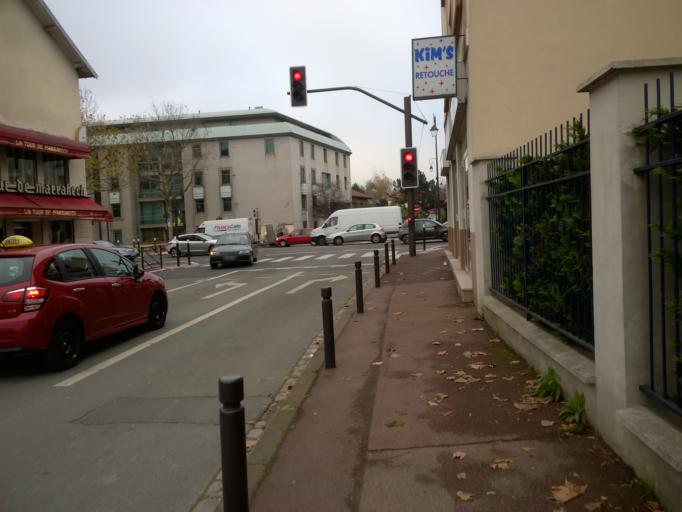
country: FR
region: Ile-de-France
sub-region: Departement des Hauts-de-Seine
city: Antony
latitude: 48.7488
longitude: 2.3036
